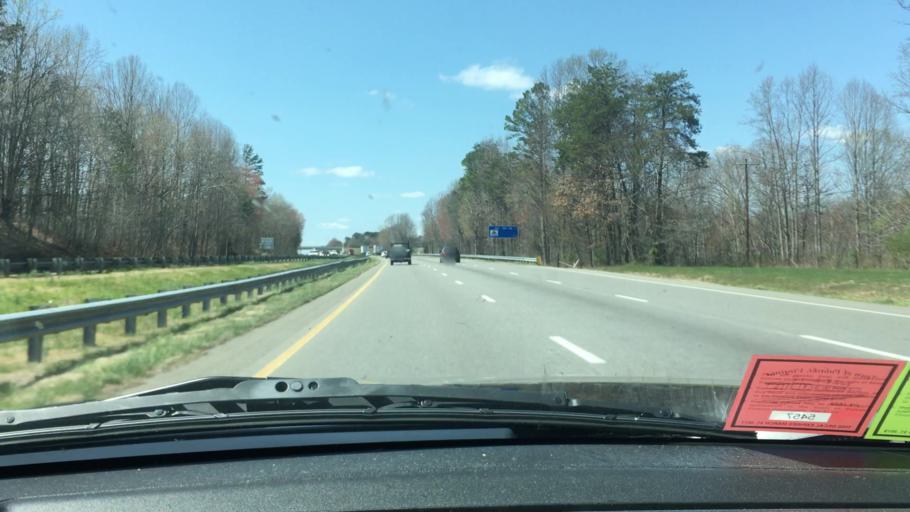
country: US
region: North Carolina
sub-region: Surry County
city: Pilot Mountain
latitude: 36.4032
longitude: -80.4935
